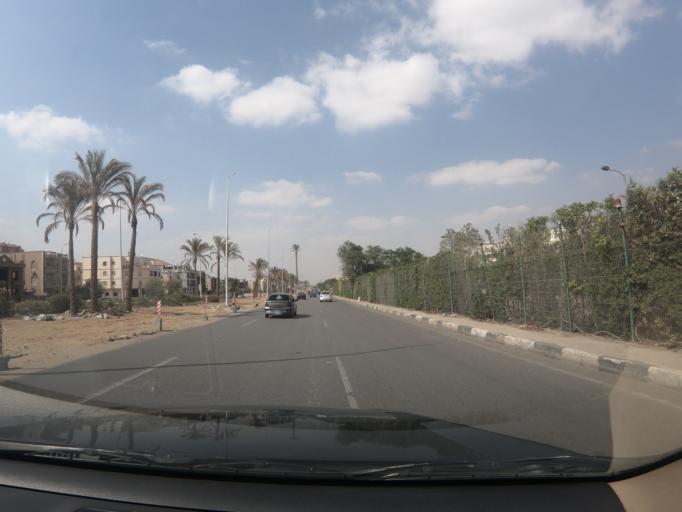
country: EG
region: Muhafazat al Qalyubiyah
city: Al Khankah
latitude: 30.0562
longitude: 31.4751
